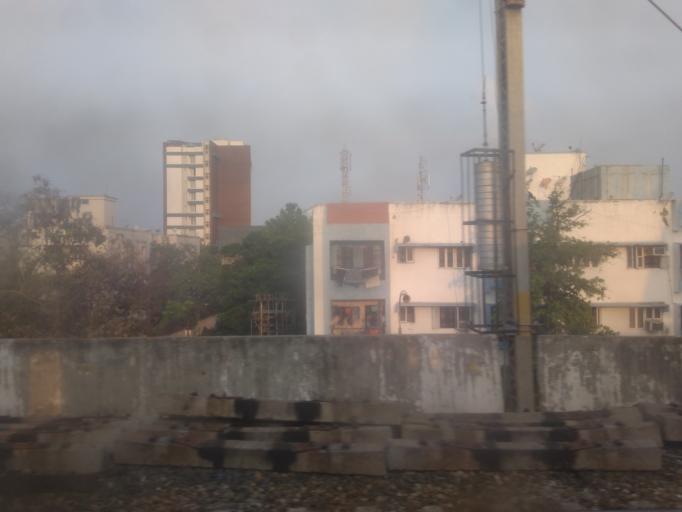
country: IN
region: Tamil Nadu
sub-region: Chennai
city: Gandhi Nagar
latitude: 13.0395
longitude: 80.2695
